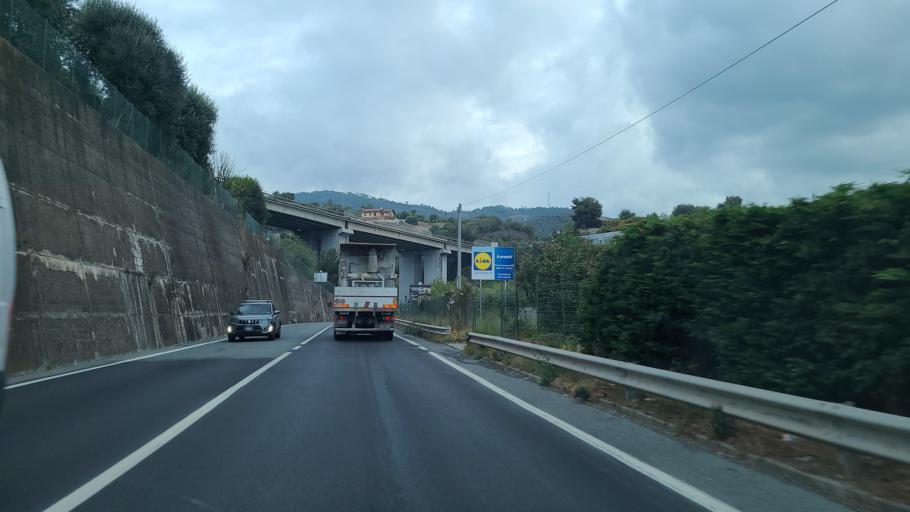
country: IT
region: Liguria
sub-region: Provincia di Imperia
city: Taggia
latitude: 43.8535
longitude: 7.8411
